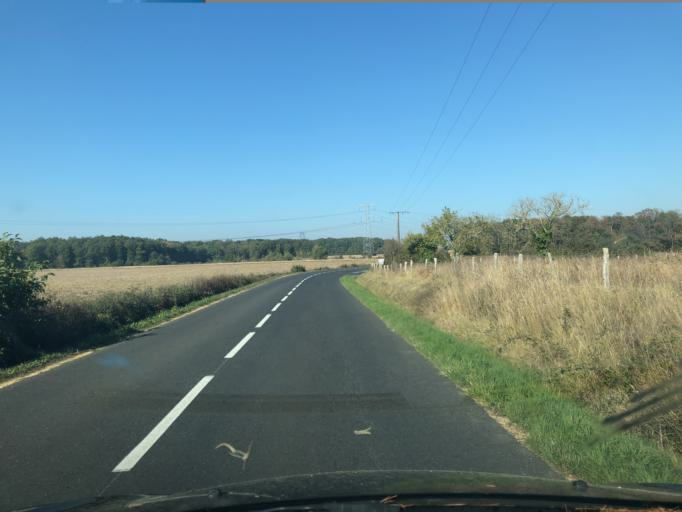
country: FR
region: Centre
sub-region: Departement d'Indre-et-Loire
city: Rouziers-de-Touraine
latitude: 47.5283
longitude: 0.6408
